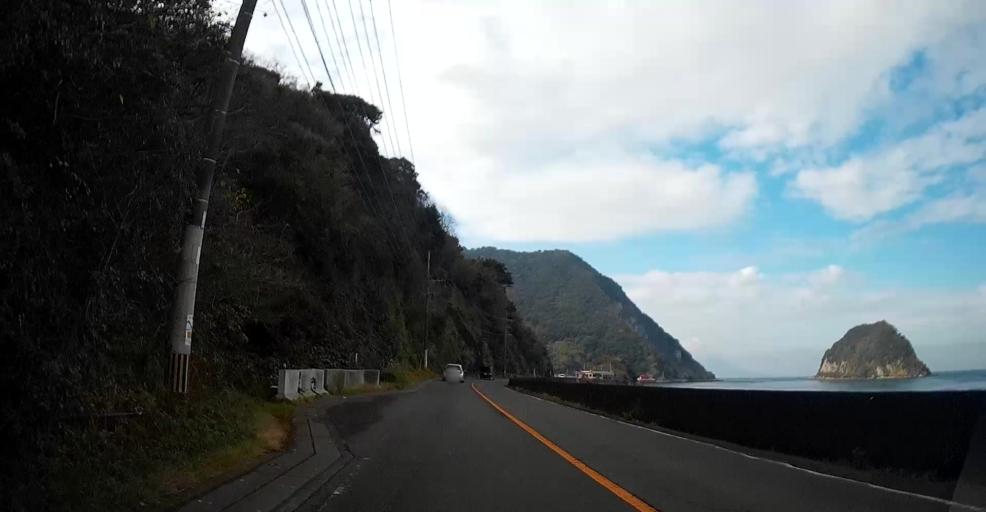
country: JP
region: Nagasaki
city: Shimabara
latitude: 32.6171
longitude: 130.4508
